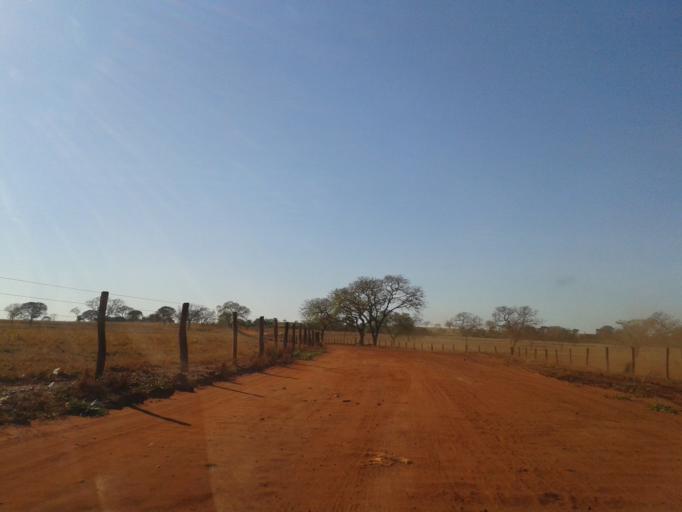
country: BR
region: Minas Gerais
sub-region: Ituiutaba
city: Ituiutaba
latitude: -18.9810
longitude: -49.4043
